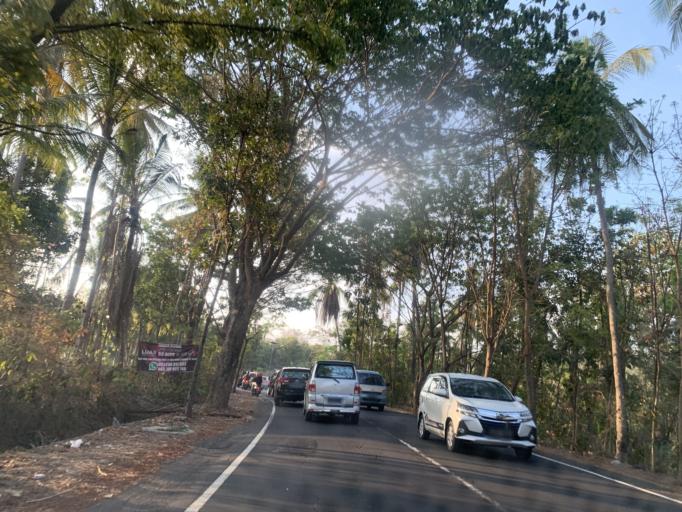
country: ID
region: Bali
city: Angkahgede
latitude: -8.4858
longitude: 114.9497
